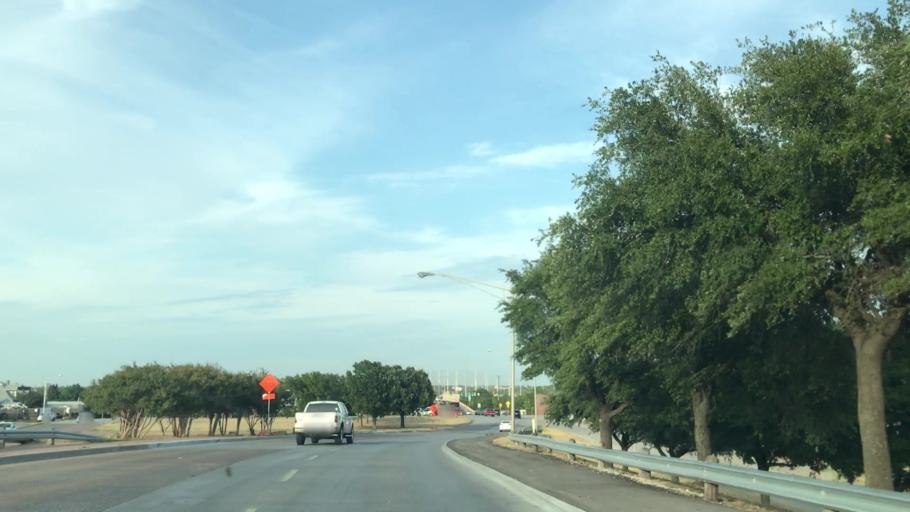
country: US
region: Texas
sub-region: Tarrant County
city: Fort Worth
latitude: 32.7604
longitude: -97.3267
